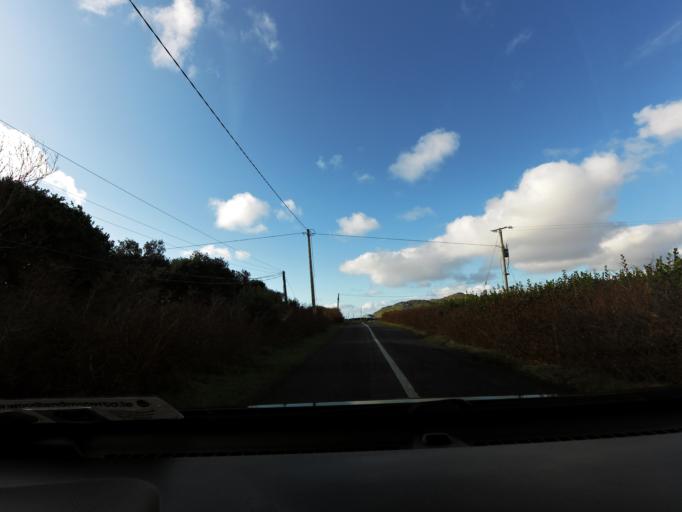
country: IE
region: Connaught
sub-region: Maigh Eo
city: Belmullet
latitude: 53.8717
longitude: -9.9252
